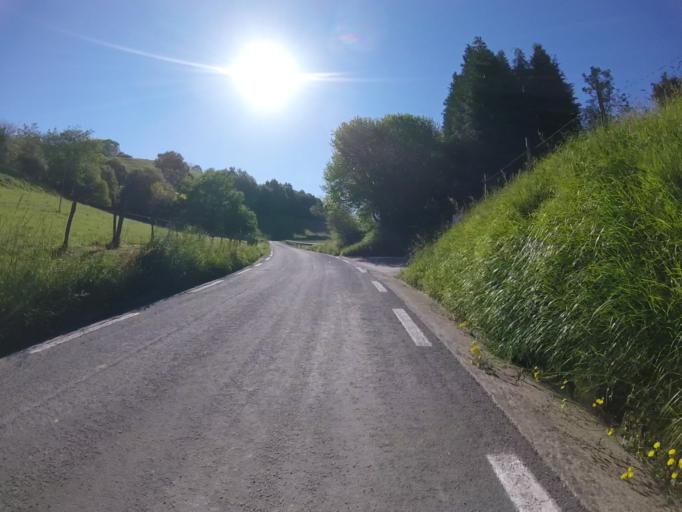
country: ES
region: Basque Country
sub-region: Provincia de Guipuzcoa
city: Aizarnazabal
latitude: 43.2311
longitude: -2.2193
